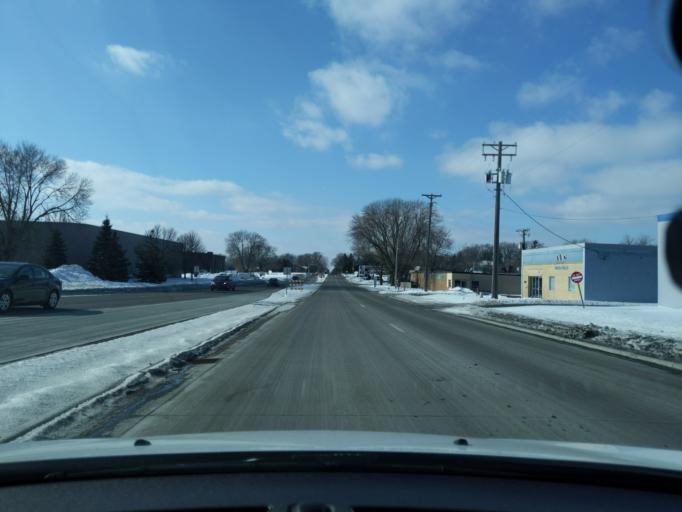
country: US
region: Minnesota
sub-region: Hennepin County
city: Saint Anthony
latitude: 45.0207
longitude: -93.2081
